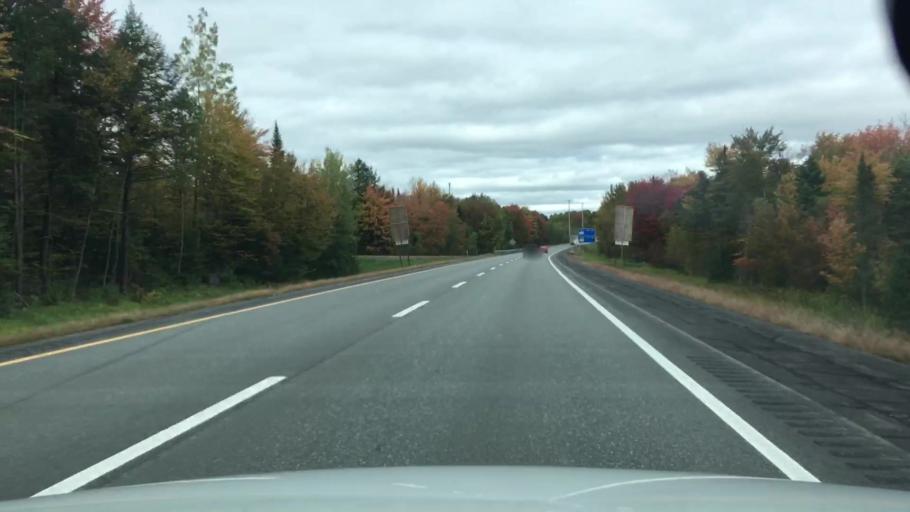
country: US
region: Maine
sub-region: Somerset County
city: Pittsfield
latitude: 44.7777
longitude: -69.4071
